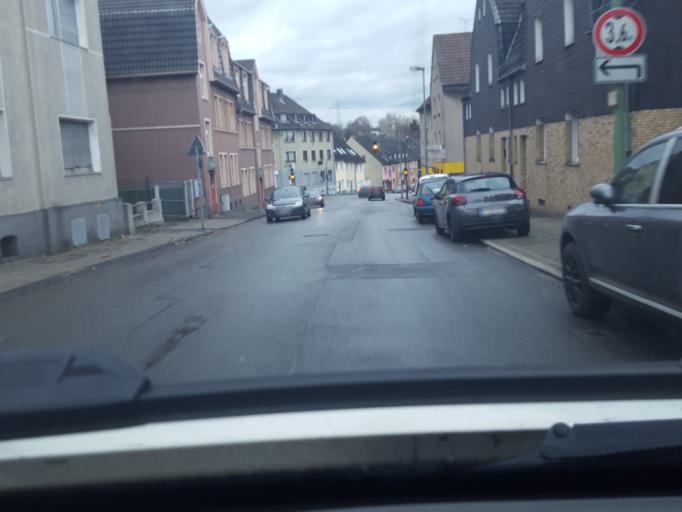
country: DE
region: North Rhine-Westphalia
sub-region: Regierungsbezirk Dusseldorf
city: Essen
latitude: 51.4670
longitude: 6.9553
